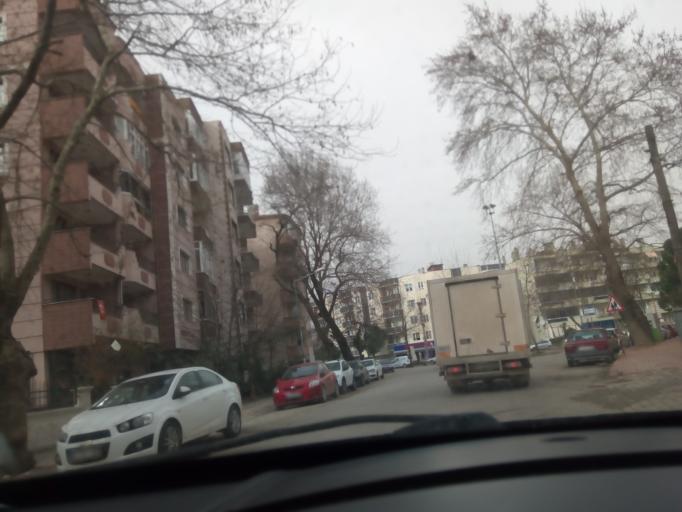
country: TR
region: Balikesir
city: Susurluk
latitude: 39.9179
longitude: 28.1537
